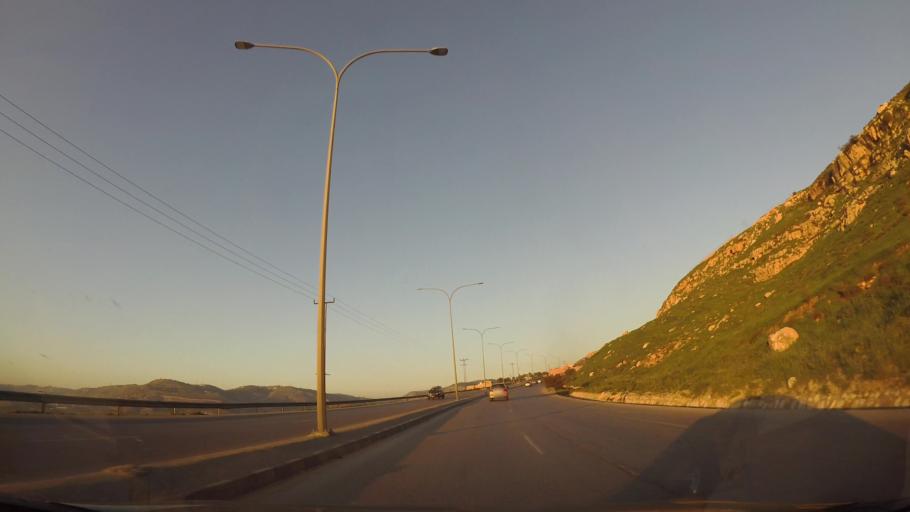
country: JO
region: Amman
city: Umm as Summaq
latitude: 31.8731
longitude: 35.7720
